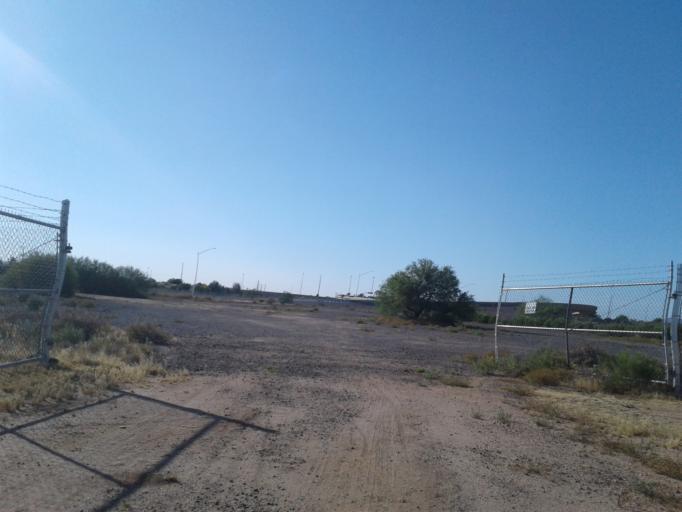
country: US
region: Arizona
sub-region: Maricopa County
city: Paradise Valley
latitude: 33.6766
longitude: -112.0069
